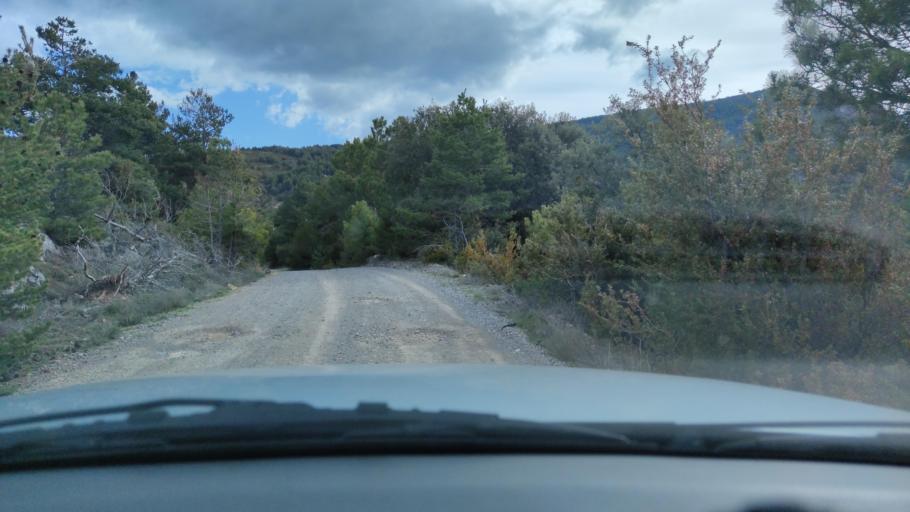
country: ES
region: Catalonia
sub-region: Provincia de Lleida
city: Coll de Nargo
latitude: 42.2512
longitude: 1.4030
